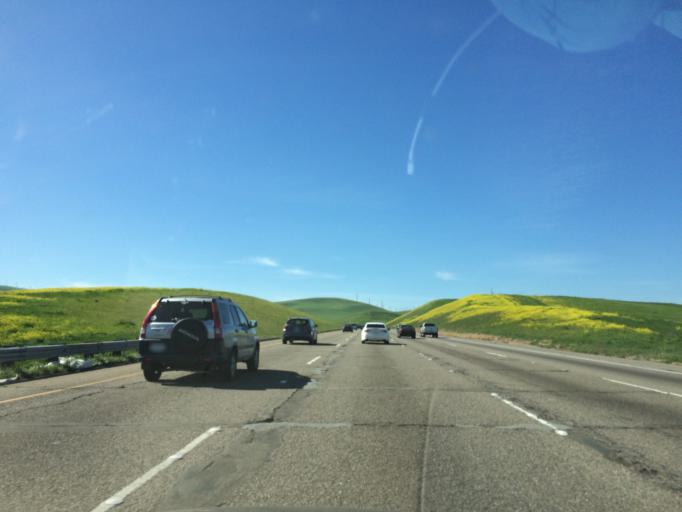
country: US
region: California
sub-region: San Joaquin County
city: Mountain House
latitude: 37.7365
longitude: -121.6173
